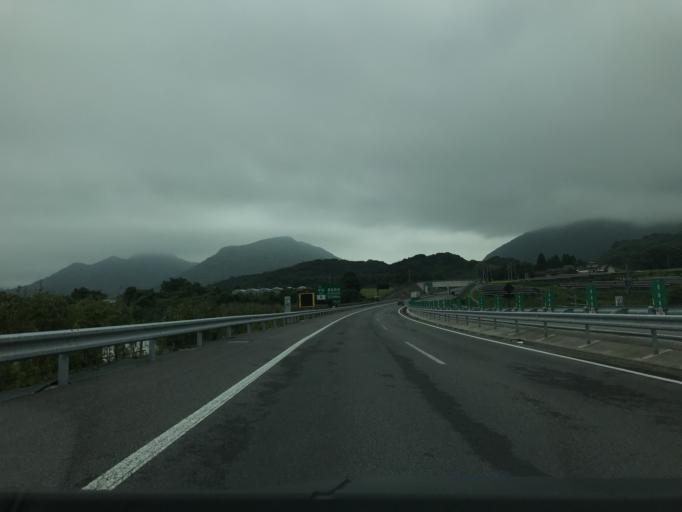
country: JP
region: Oita
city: Bungo-Takada-shi
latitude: 33.5027
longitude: 131.3122
